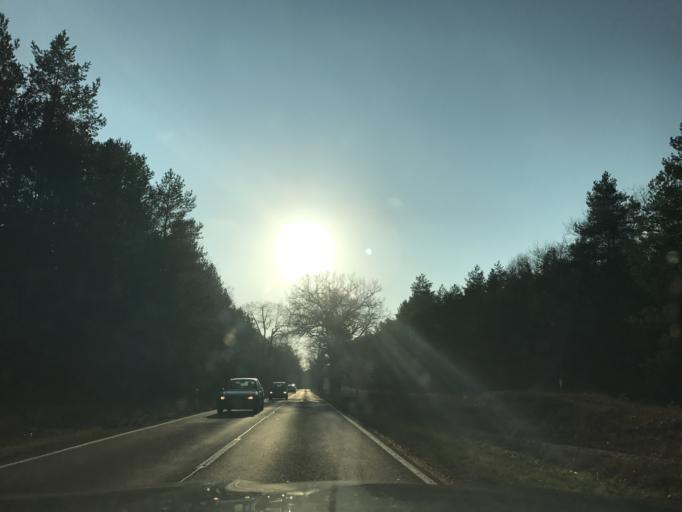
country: DE
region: Brandenburg
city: Brandenburg an der Havel
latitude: 52.3616
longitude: 12.5021
